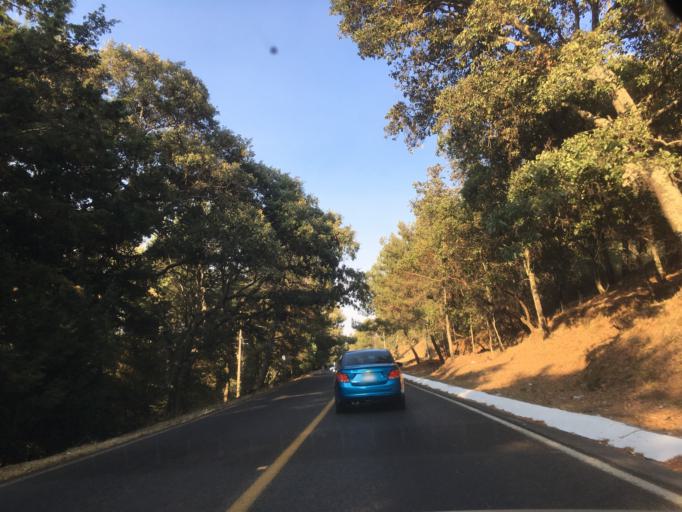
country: MX
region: Michoacan
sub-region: Morelia
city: Iratzio
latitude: 19.6290
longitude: -101.4542
